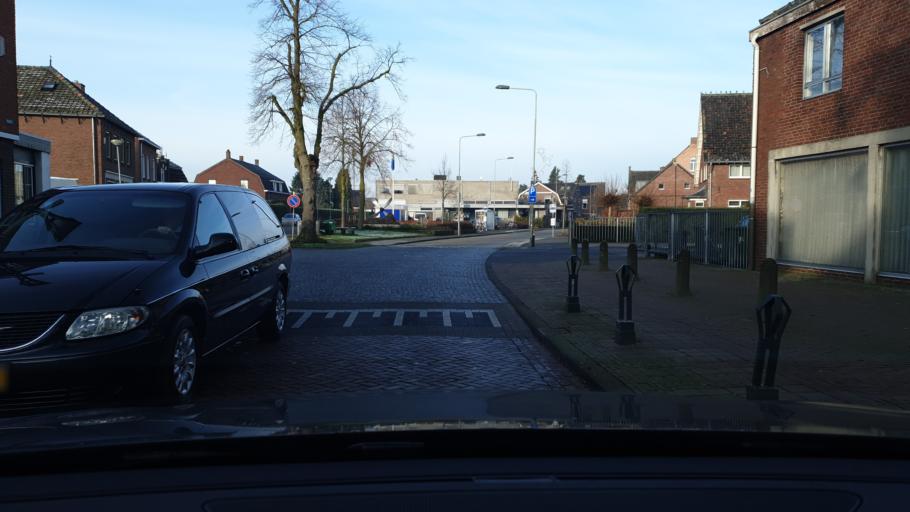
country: NL
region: Limburg
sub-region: Gemeente Peel en Maas
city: Maasbree
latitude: 51.4127
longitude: 6.0351
